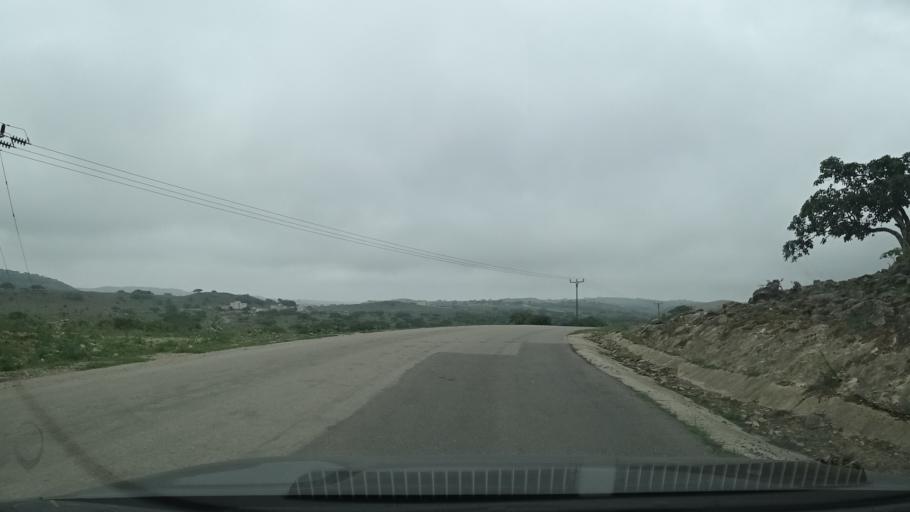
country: OM
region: Zufar
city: Salalah
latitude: 17.1195
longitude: 54.5665
